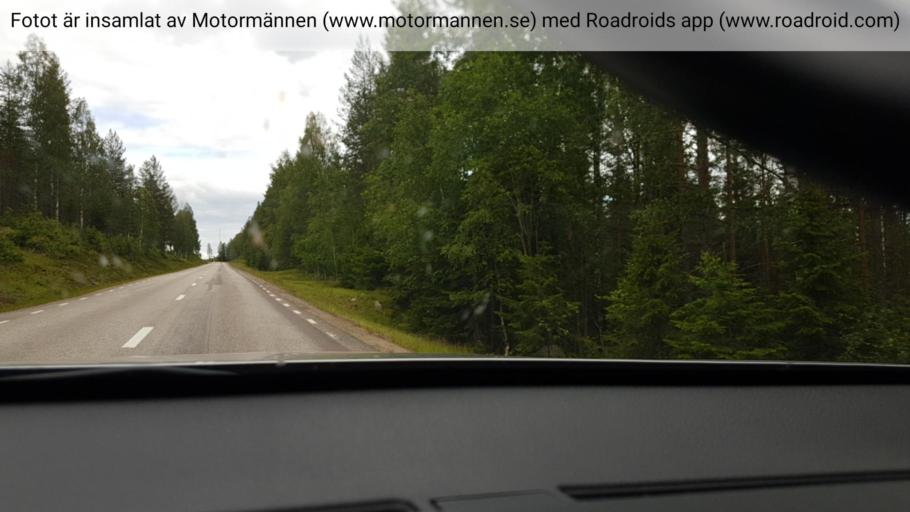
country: NO
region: Hedmark
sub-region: Trysil
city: Innbygda
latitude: 61.0287
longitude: 12.4841
